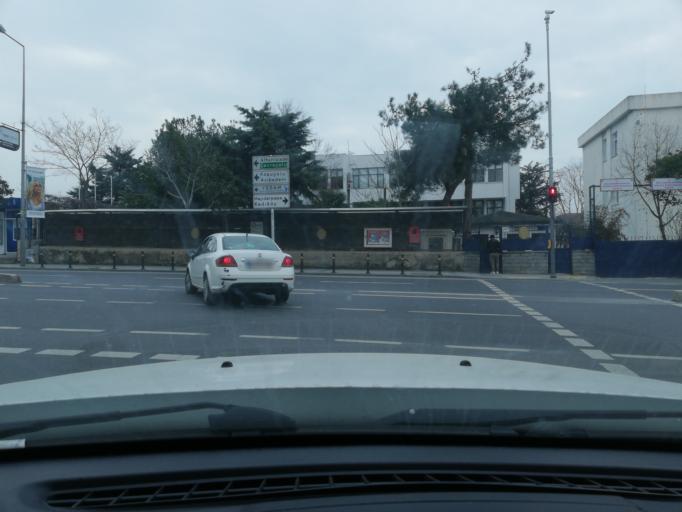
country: TR
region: Istanbul
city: UEskuedar
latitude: 41.0151
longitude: 29.0281
